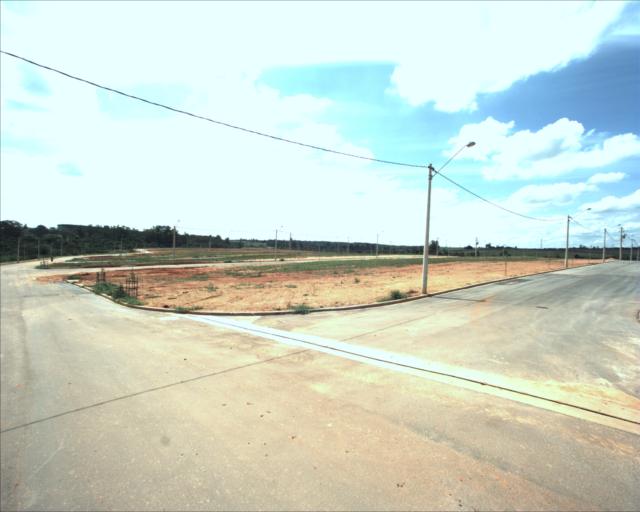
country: BR
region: Sao Paulo
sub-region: Sorocaba
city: Sorocaba
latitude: -23.4072
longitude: -47.4088
